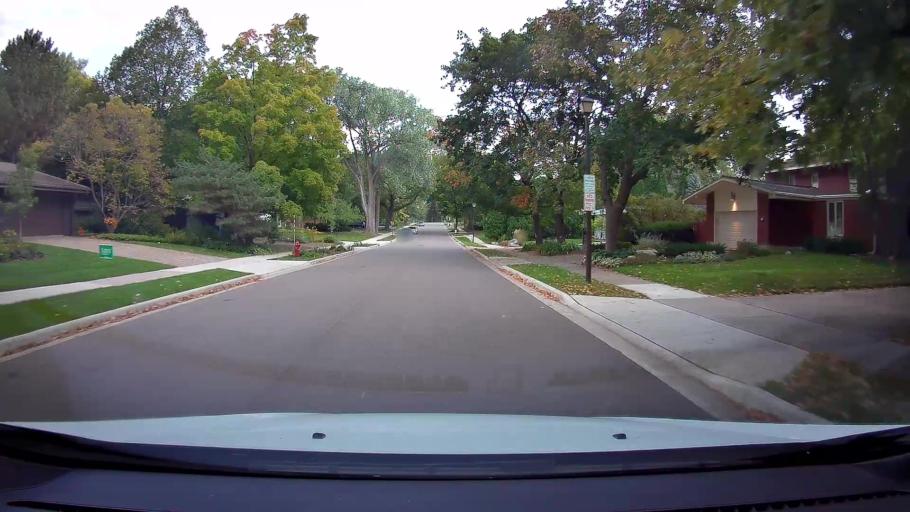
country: US
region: Minnesota
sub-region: Ramsey County
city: Lauderdale
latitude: 44.9892
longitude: -93.1911
